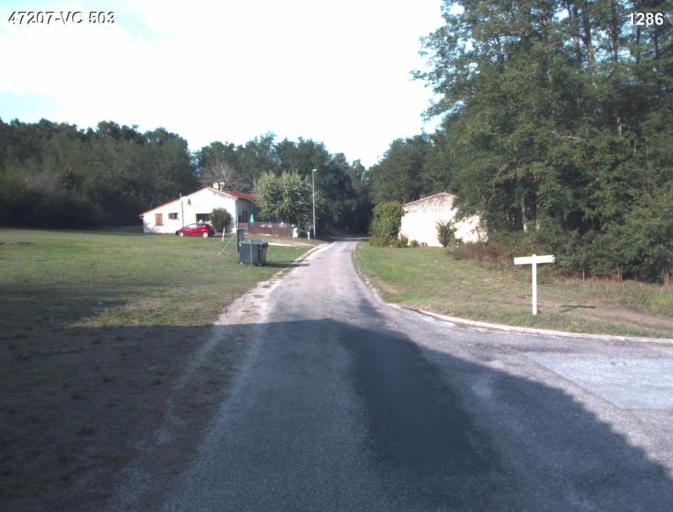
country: FR
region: Aquitaine
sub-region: Departement du Lot-et-Garonne
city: Barbaste
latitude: 44.1954
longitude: 0.2313
